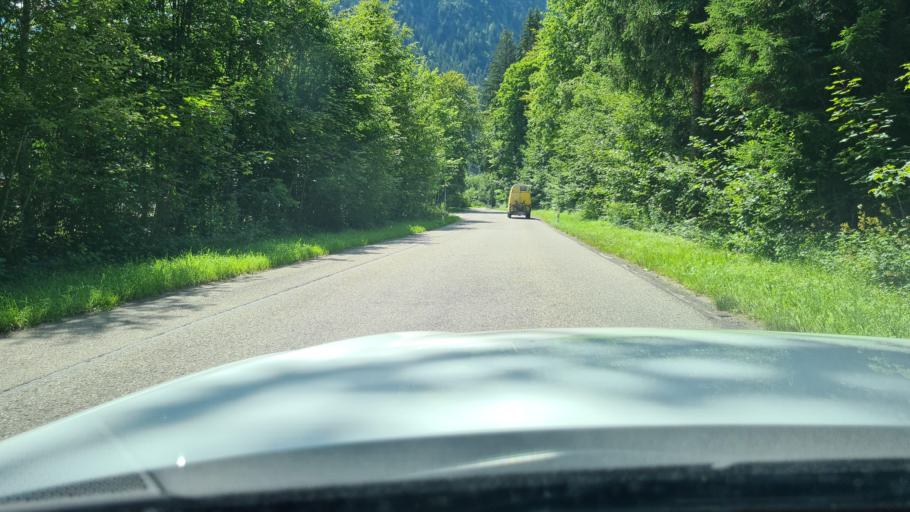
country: DE
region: Bavaria
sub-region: Swabia
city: Oberstdorf
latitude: 47.3846
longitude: 10.2812
